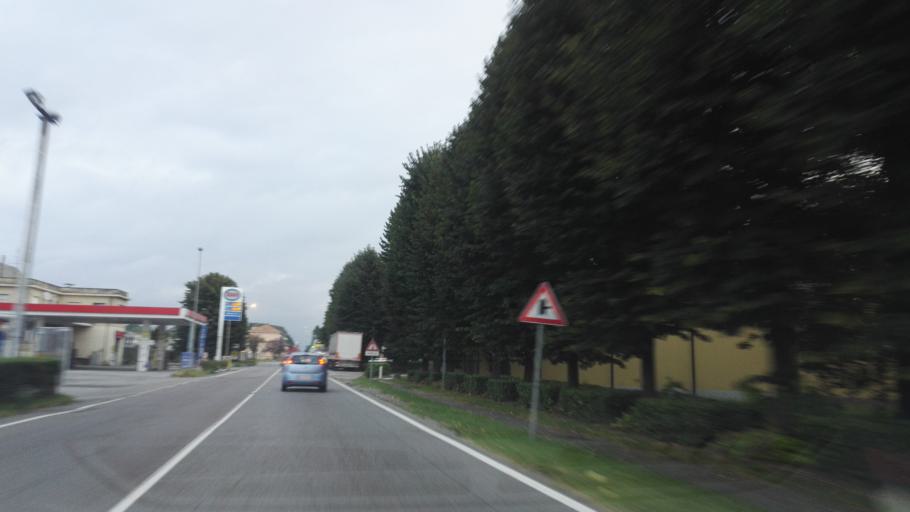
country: IT
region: Lombardy
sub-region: Citta metropolitana di Milano
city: Caleppio
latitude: 45.4332
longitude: 9.3788
